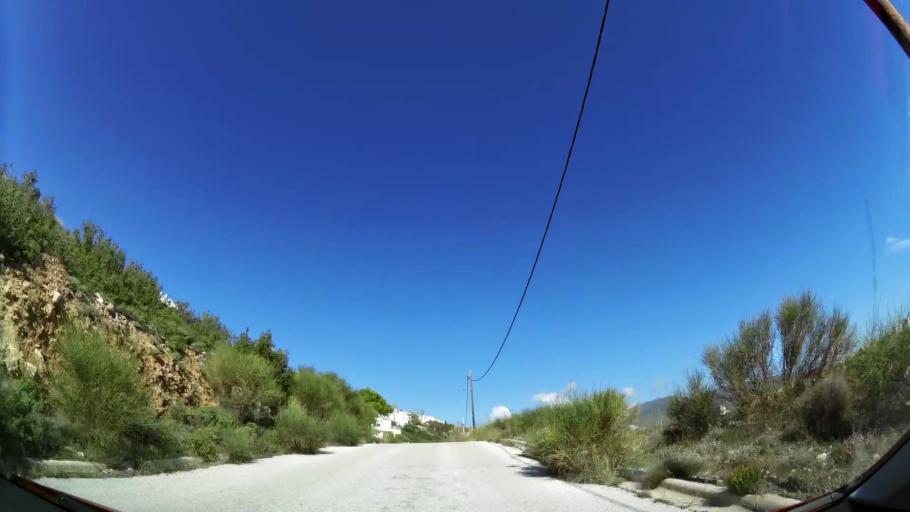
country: GR
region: Attica
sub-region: Nomarchia Anatolikis Attikis
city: Dhrafi
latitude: 38.0222
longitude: 23.8977
